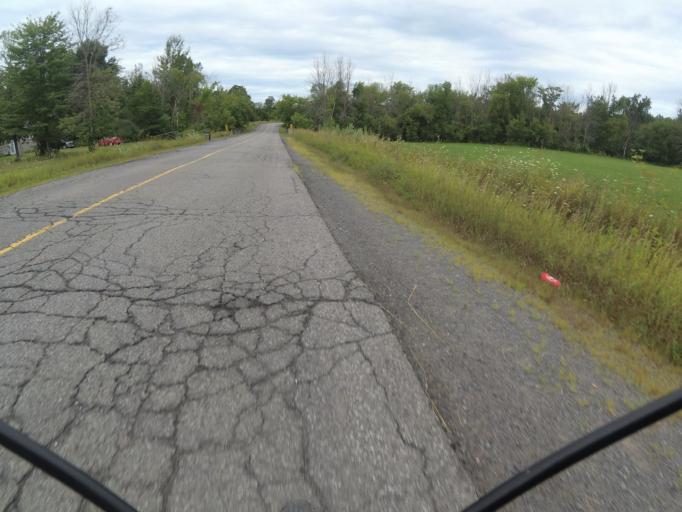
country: CA
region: Ontario
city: Bourget
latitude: 45.3988
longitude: -75.2840
